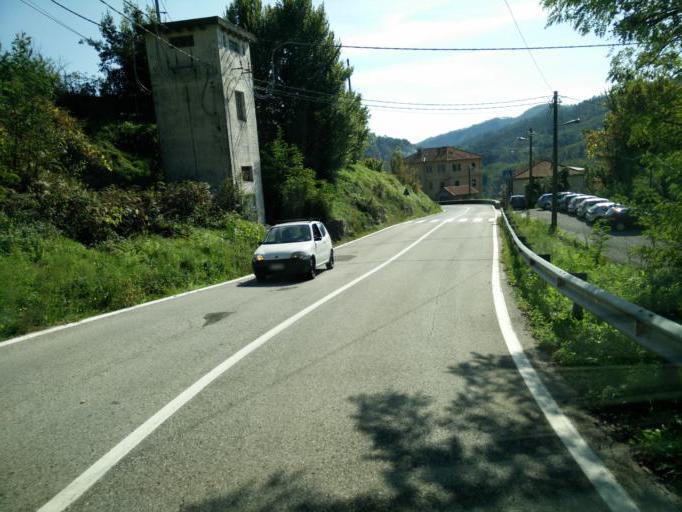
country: IT
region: Liguria
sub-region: Provincia di La Spezia
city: Carrodano
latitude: 44.2440
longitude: 9.6548
